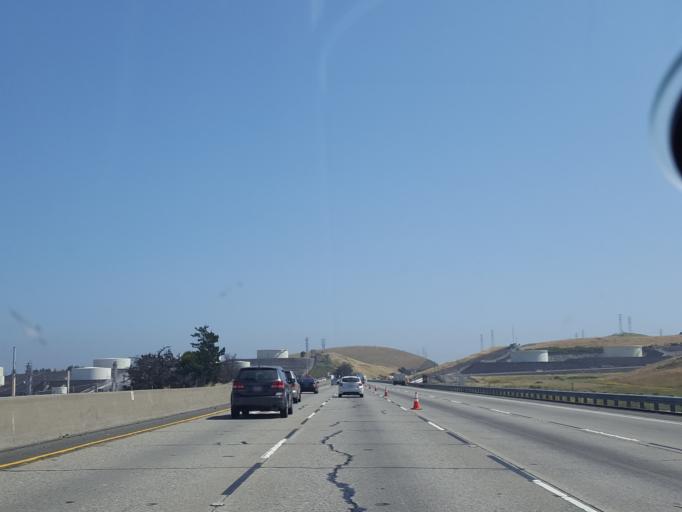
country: US
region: California
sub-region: Contra Costa County
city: Rodeo
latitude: 38.0330
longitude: -122.2526
